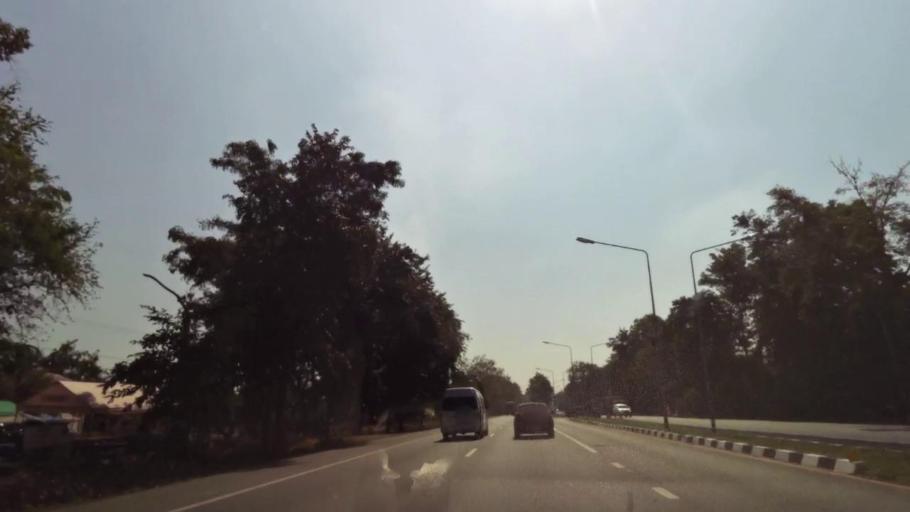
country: TH
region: Phichit
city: Bueng Na Rang
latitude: 16.0639
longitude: 100.1233
